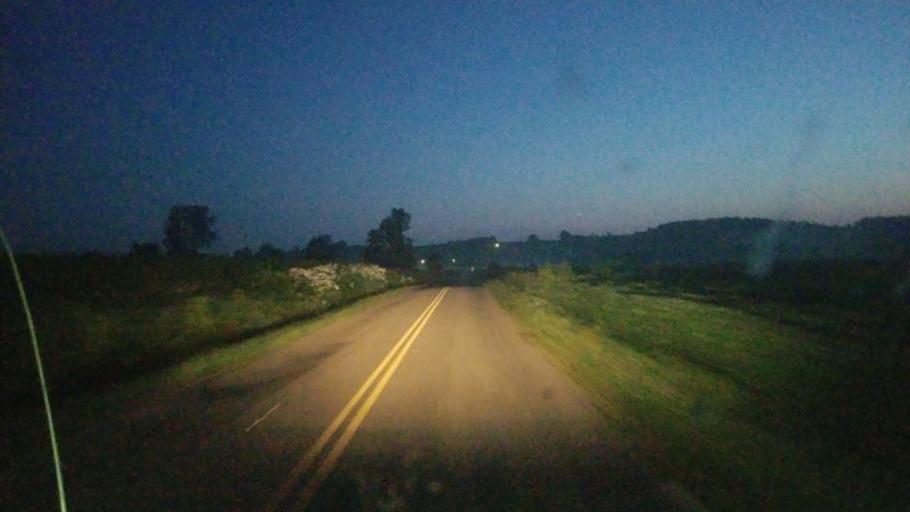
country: US
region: Ohio
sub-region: Perry County
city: Thornport
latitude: 39.9136
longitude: -82.3373
